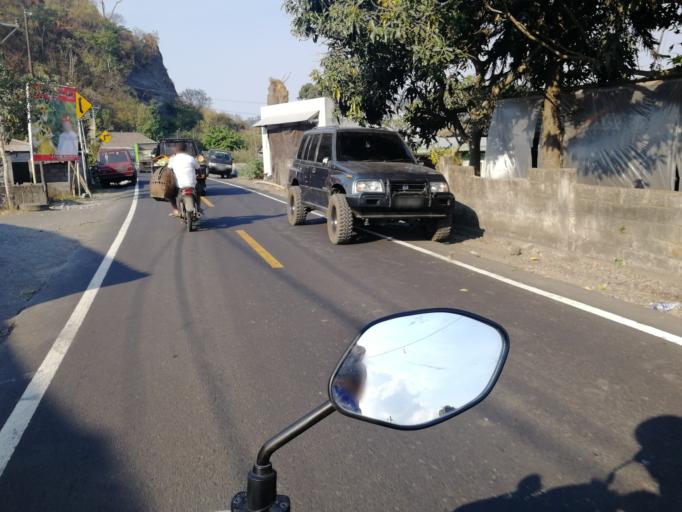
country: ID
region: Bali
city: Banjar Trunyan
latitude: -8.2409
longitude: 115.4047
